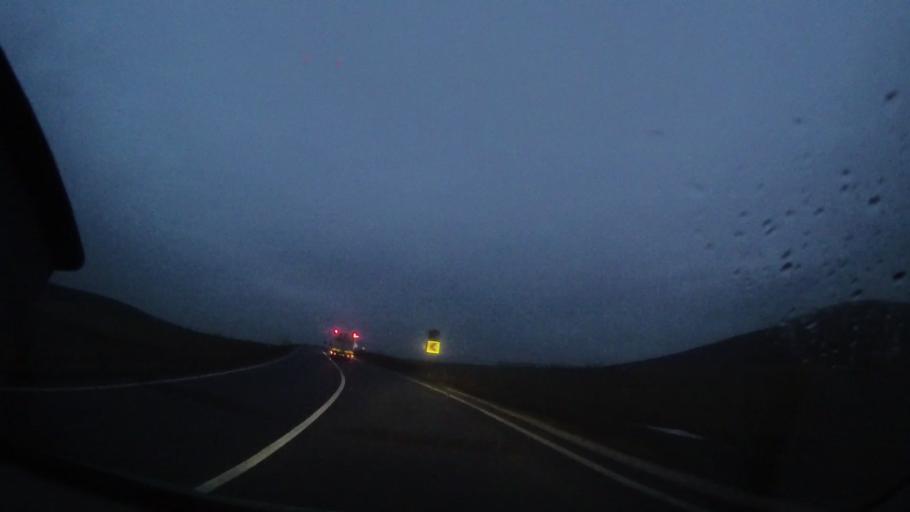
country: RO
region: Harghita
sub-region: Comuna Subcetate
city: Subcetate
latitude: 46.8450
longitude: 25.4718
